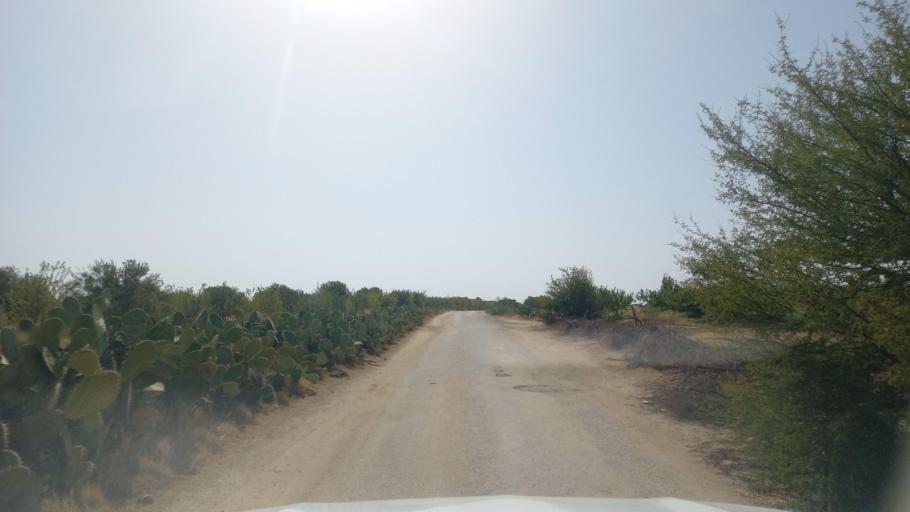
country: TN
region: Al Qasrayn
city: Kasserine
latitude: 35.2461
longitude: 9.0301
